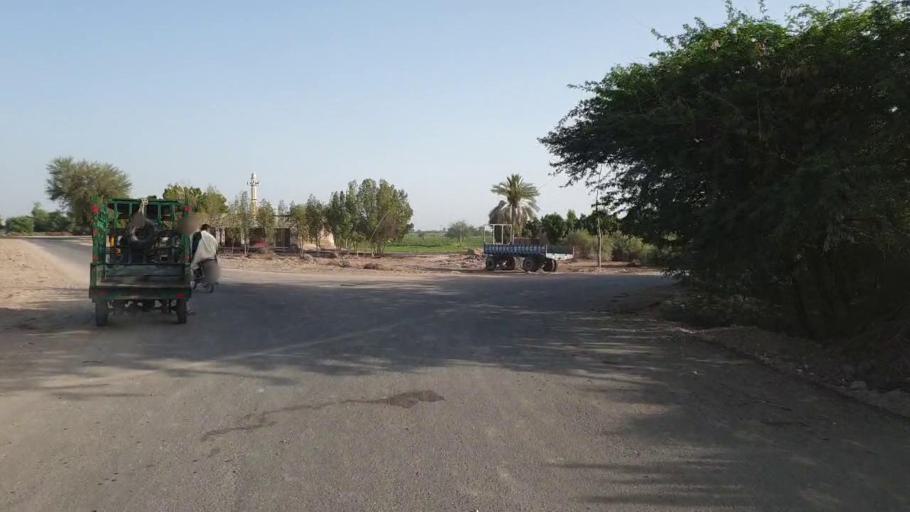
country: PK
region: Sindh
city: Jam Sahib
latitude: 26.3447
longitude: 68.5685
